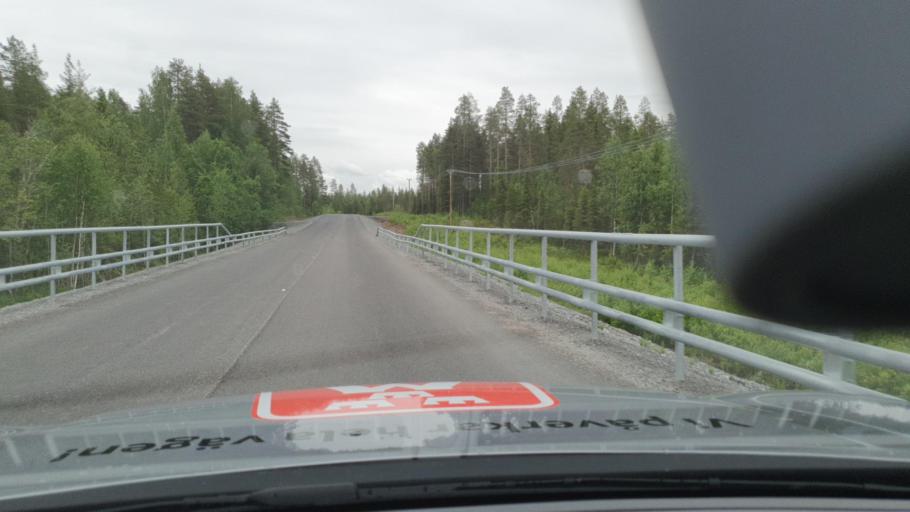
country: SE
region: Norrbotten
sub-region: Overtornea Kommun
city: OEvertornea
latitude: 66.6431
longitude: 23.2476
